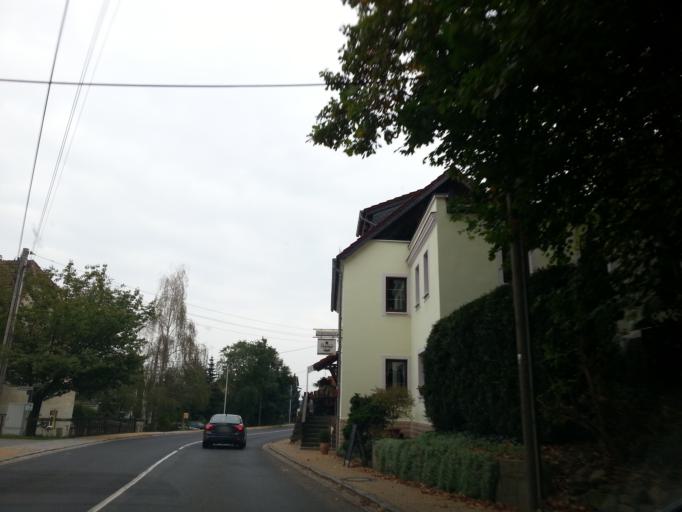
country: DE
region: Saxony
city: Coswig
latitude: 51.1024
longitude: 13.5815
